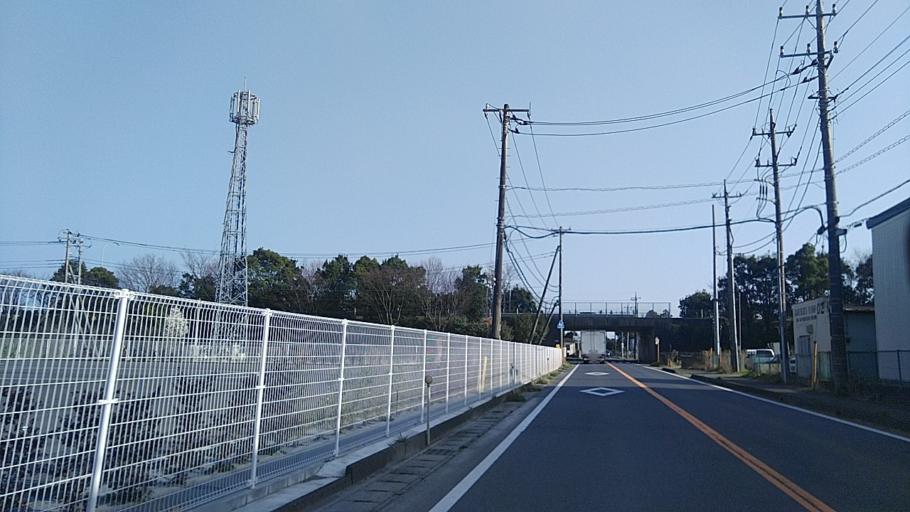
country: JP
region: Chiba
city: Narita
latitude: 35.8128
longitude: 140.4000
